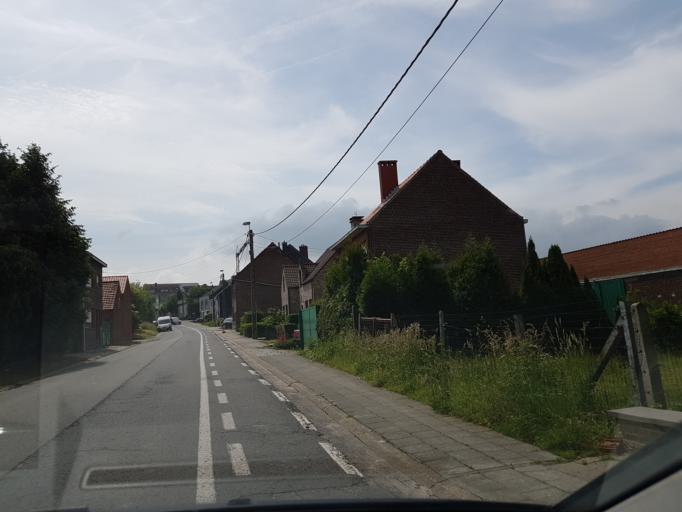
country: BE
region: Flanders
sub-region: Provincie Vlaams-Brabant
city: Asse
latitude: 50.9205
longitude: 4.1553
